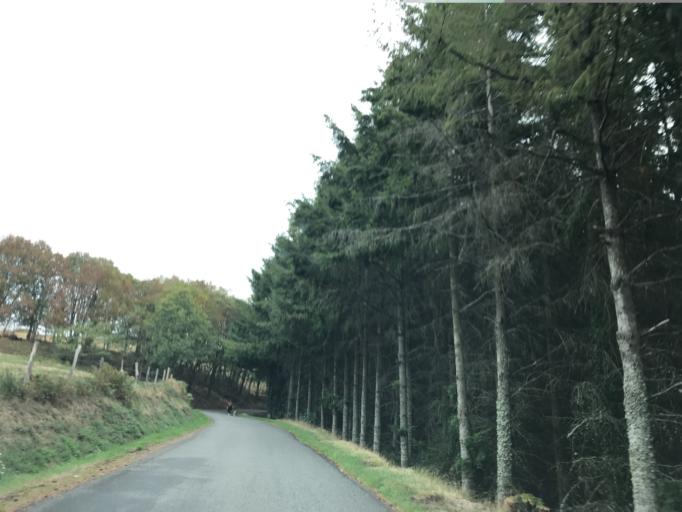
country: FR
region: Auvergne
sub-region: Departement du Puy-de-Dome
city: Thiers
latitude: 45.8384
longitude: 3.5575
